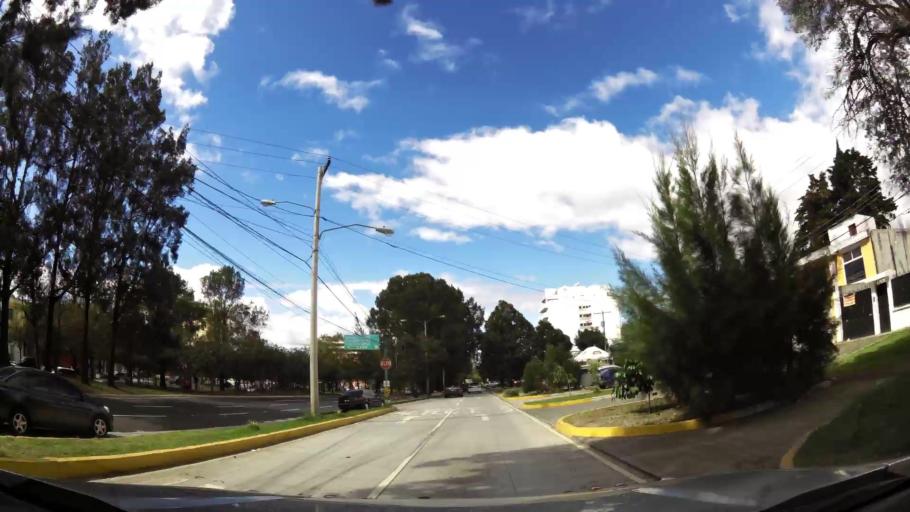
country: GT
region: Guatemala
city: Santa Catarina Pinula
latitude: 14.5930
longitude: -90.4931
